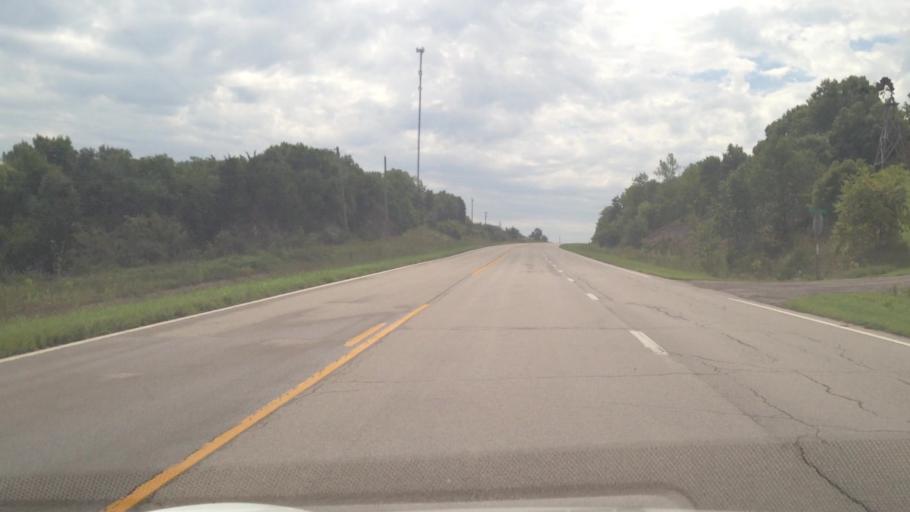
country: US
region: Kansas
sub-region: Bourbon County
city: Fort Scott
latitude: 37.8319
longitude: -94.9808
